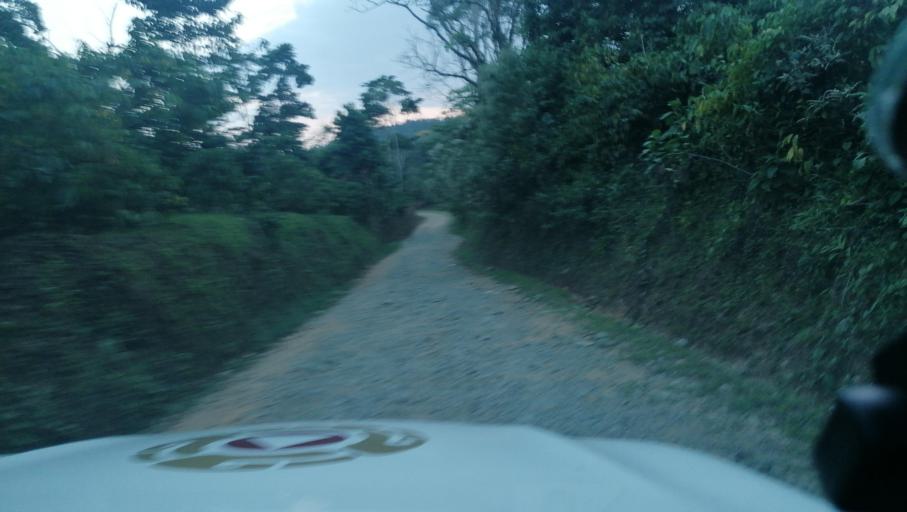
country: MX
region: Chiapas
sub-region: Cacahoatan
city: Benito Juarez
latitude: 15.0567
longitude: -92.2425
